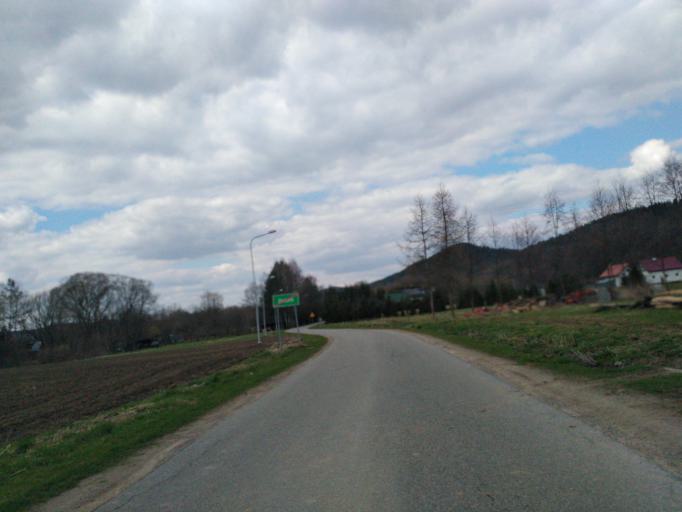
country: PL
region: Subcarpathian Voivodeship
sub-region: Powiat sanocki
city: Tyrawa Woloska
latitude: 49.6570
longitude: 22.3015
